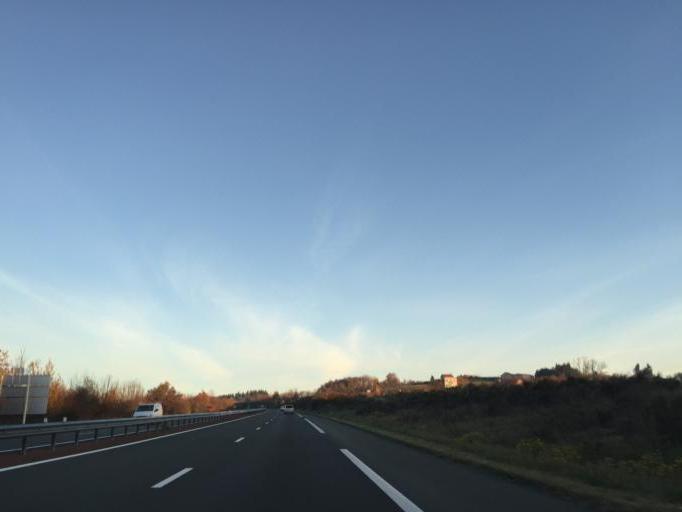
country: FR
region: Rhone-Alpes
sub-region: Departement de la Loire
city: Neulise
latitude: 45.9116
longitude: 4.1687
